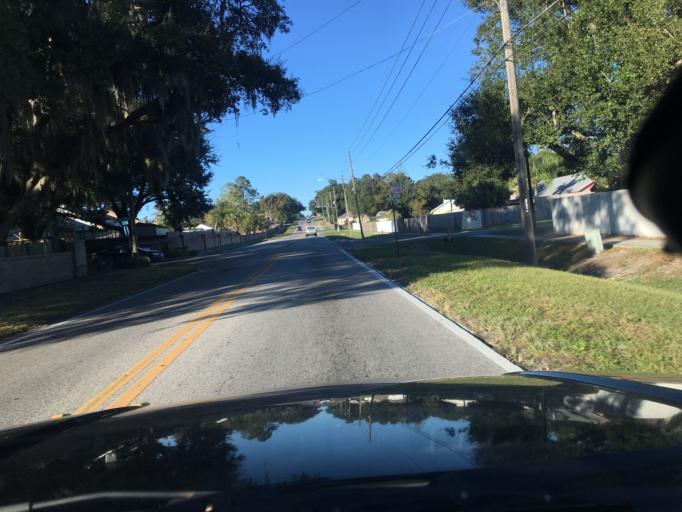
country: US
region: Florida
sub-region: Orange County
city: Lockhart
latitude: 28.5983
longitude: -81.4679
